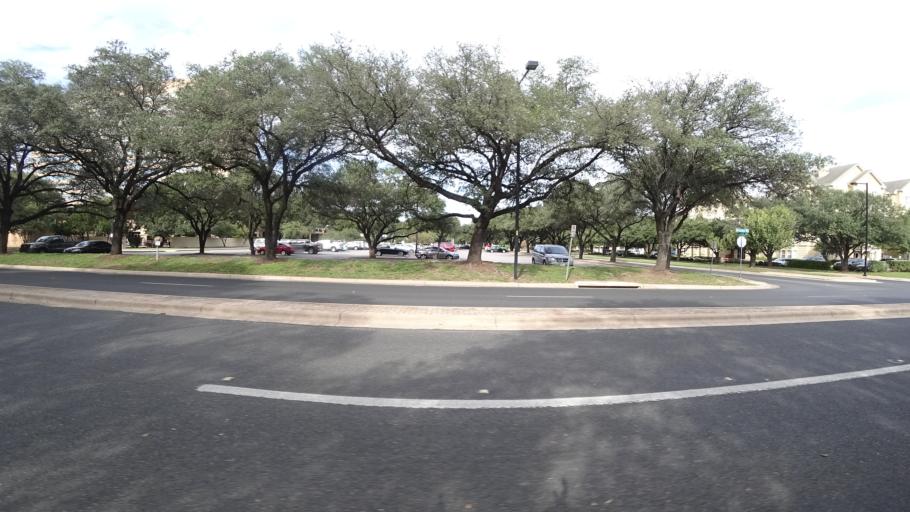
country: US
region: Texas
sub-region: Travis County
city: Austin
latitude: 30.2134
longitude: -97.7507
